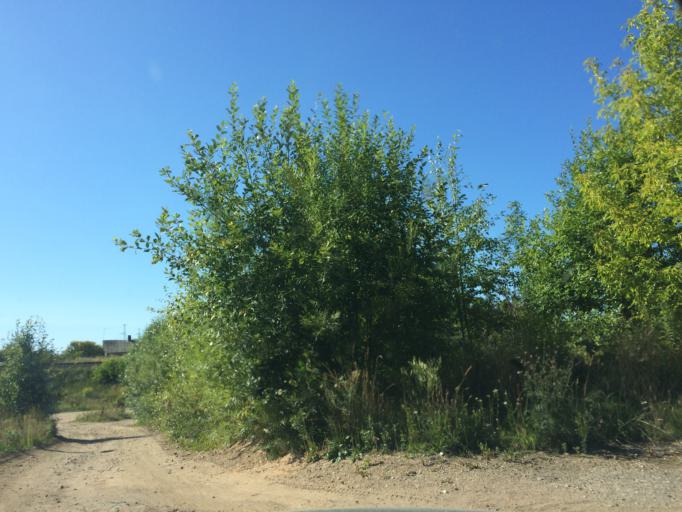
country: LV
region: Rezekne
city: Rezekne
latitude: 56.5116
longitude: 27.3217
